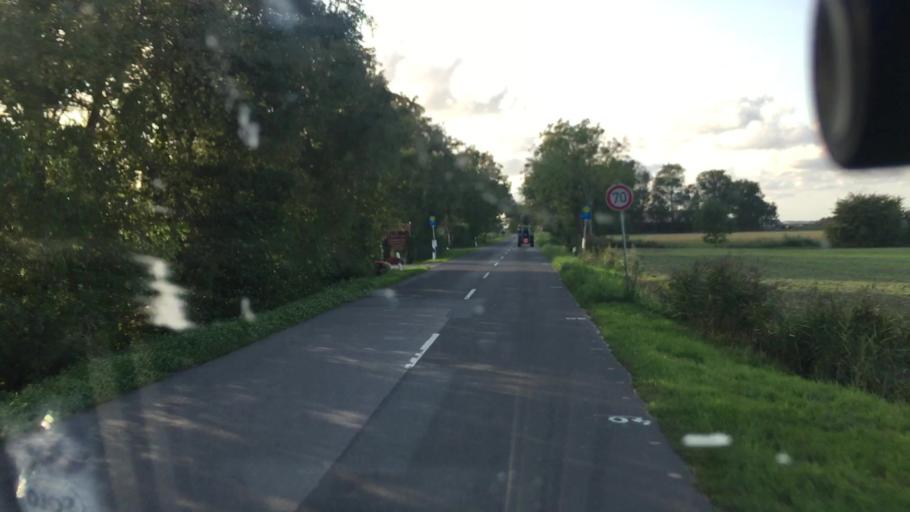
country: DE
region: Lower Saxony
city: Werdum
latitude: 53.6664
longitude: 7.7315
